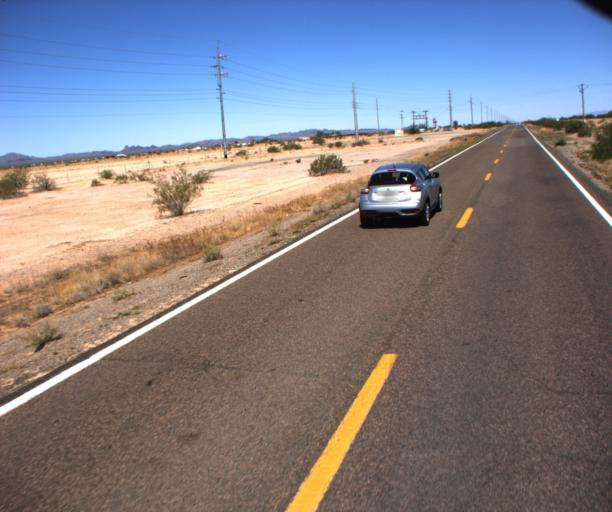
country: US
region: Arizona
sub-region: La Paz County
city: Salome
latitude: 33.8499
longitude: -113.9027
